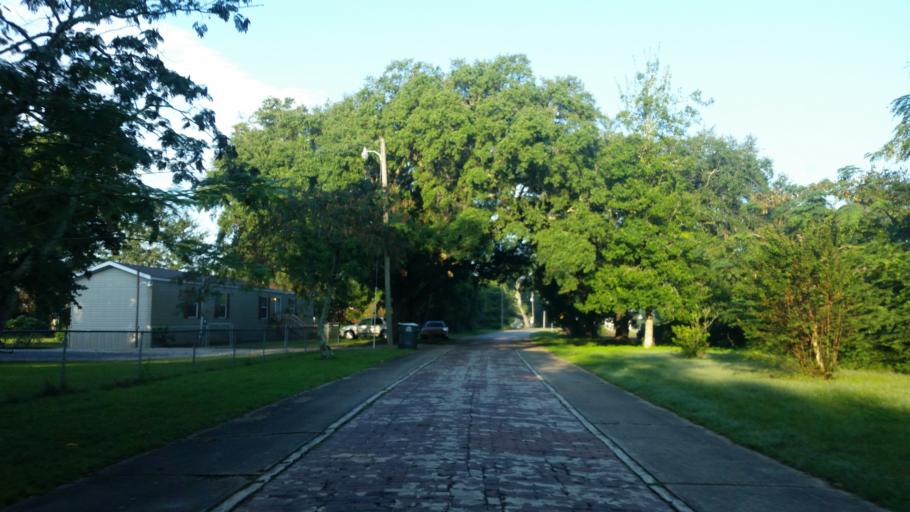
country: US
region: Florida
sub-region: Santa Rosa County
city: East Milton
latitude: 30.6252
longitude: -87.0181
